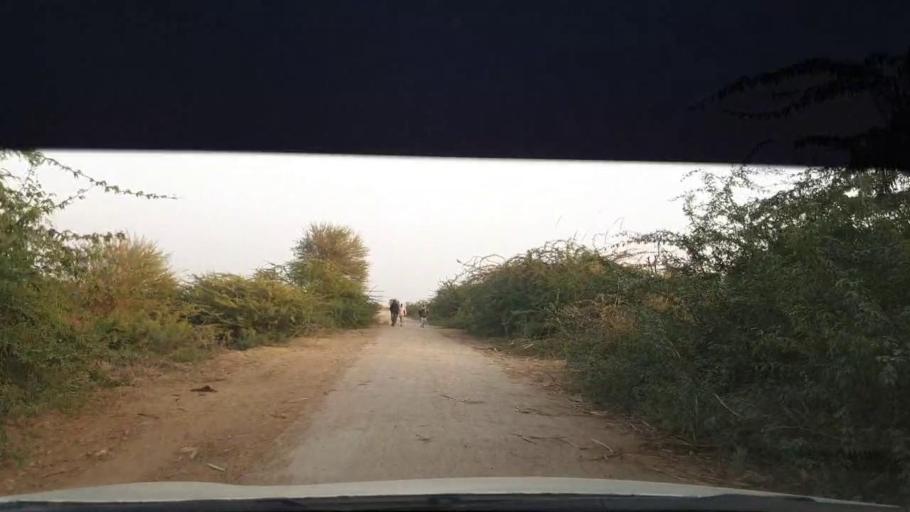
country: PK
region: Sindh
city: Berani
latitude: 25.7575
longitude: 68.9960
